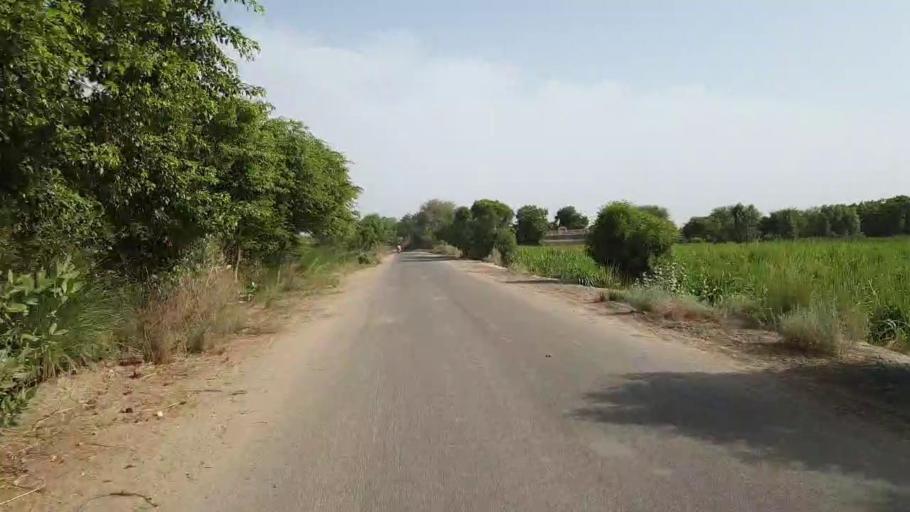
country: PK
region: Sindh
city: Sakrand
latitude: 26.2539
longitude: 68.2847
